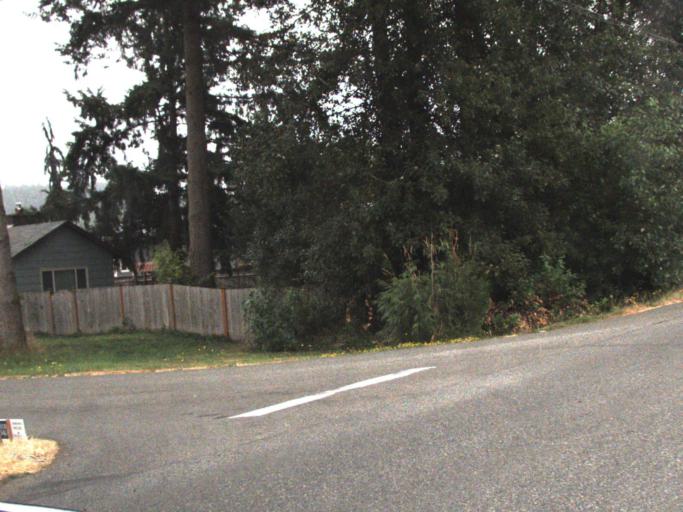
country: US
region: Washington
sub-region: King County
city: Carnation
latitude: 47.6588
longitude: -121.9103
